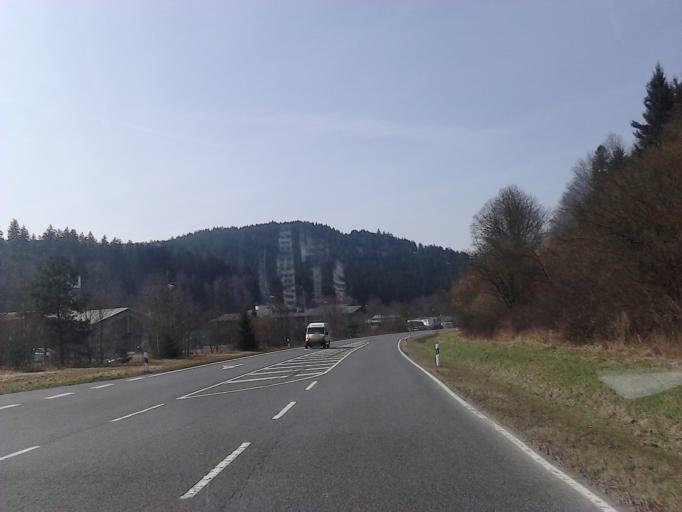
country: DE
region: Bavaria
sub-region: Upper Franconia
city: Steinwiesen
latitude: 50.2772
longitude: 11.4460
